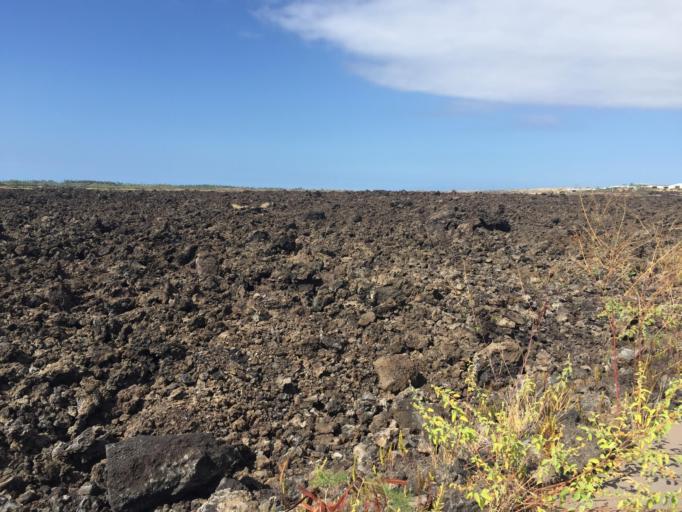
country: US
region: Hawaii
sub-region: Hawaii County
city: Kailua-Kona
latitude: 19.6786
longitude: -156.0223
